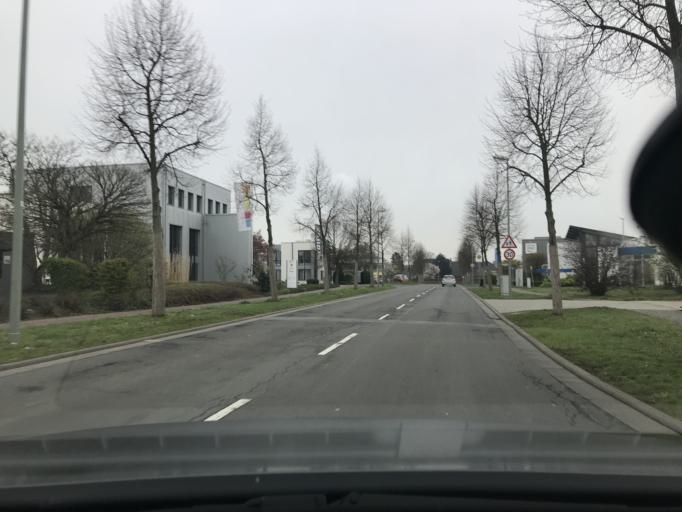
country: DE
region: North Rhine-Westphalia
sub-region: Regierungsbezirk Dusseldorf
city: Krefeld
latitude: 51.3703
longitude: 6.6392
